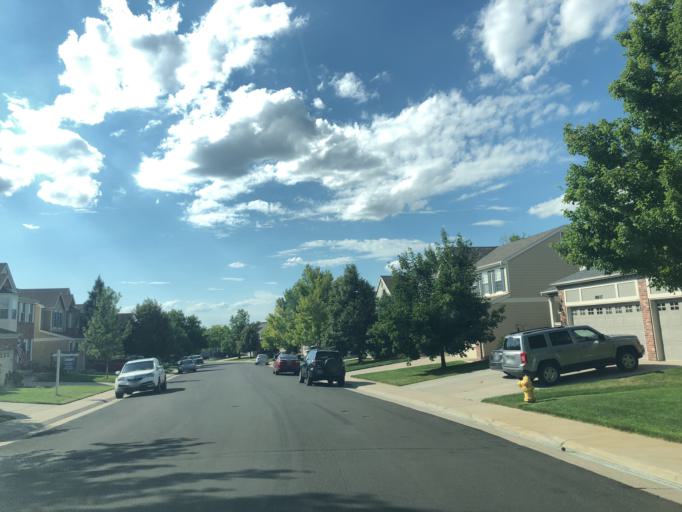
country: US
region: Colorado
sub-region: Arapahoe County
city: Dove Valley
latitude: 39.6137
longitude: -104.7705
